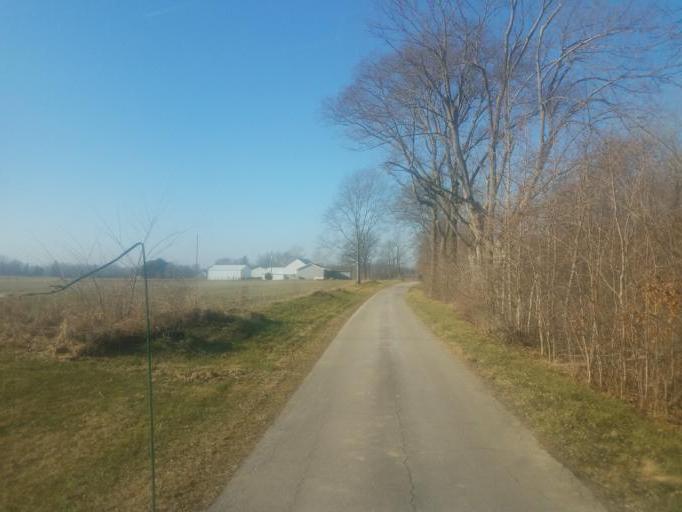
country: US
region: Ohio
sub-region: Seneca County
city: Tiffin
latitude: 41.0619
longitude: -83.0261
